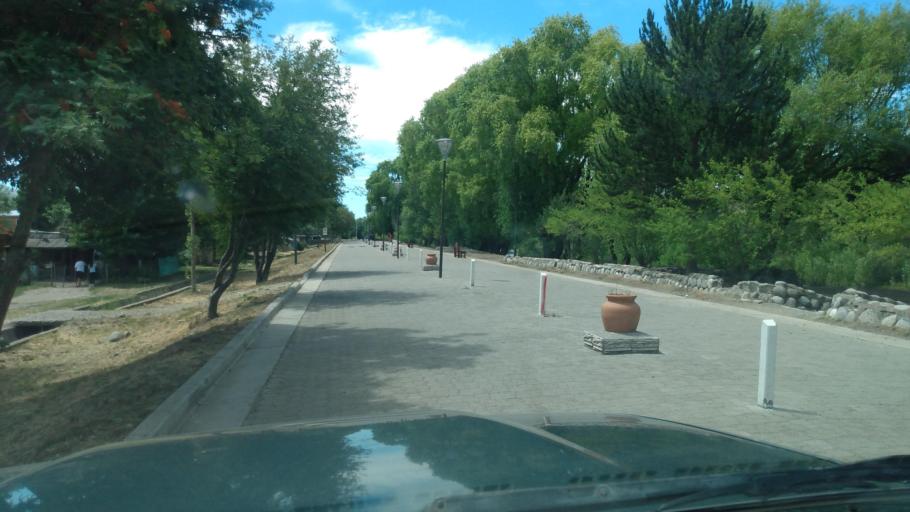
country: AR
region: Neuquen
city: Junin de los Andes
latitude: -39.9479
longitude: -71.0651
